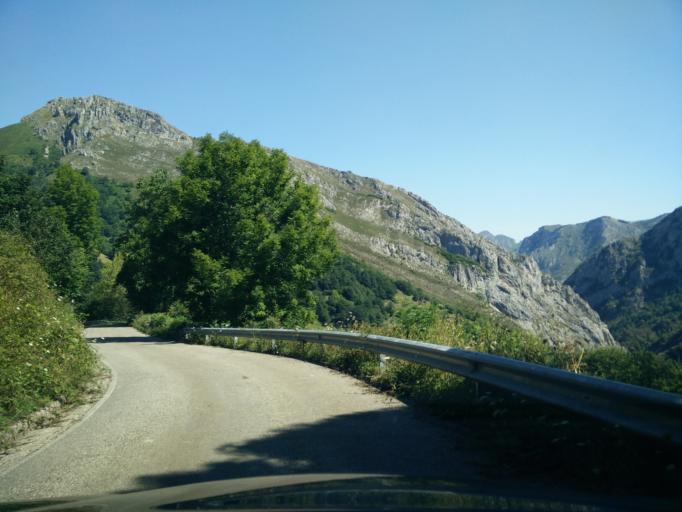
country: ES
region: Asturias
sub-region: Province of Asturias
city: Amieva
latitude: 43.1948
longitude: -5.1257
